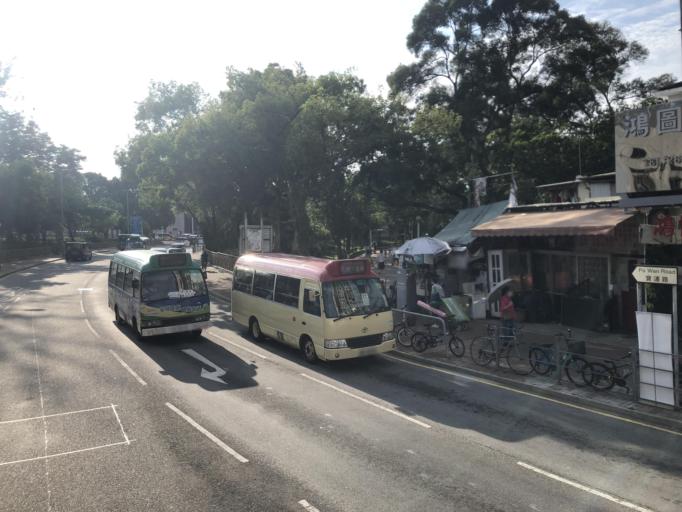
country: HK
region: Tai Po
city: Tai Po
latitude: 22.5054
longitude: 114.1268
